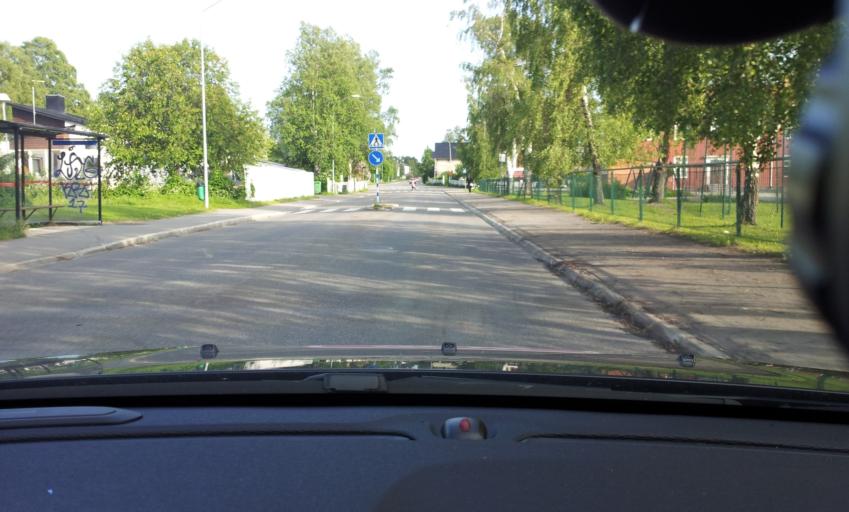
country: SE
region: Jaemtland
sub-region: OEstersunds Kommun
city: Ostersund
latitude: 63.1730
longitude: 14.6550
